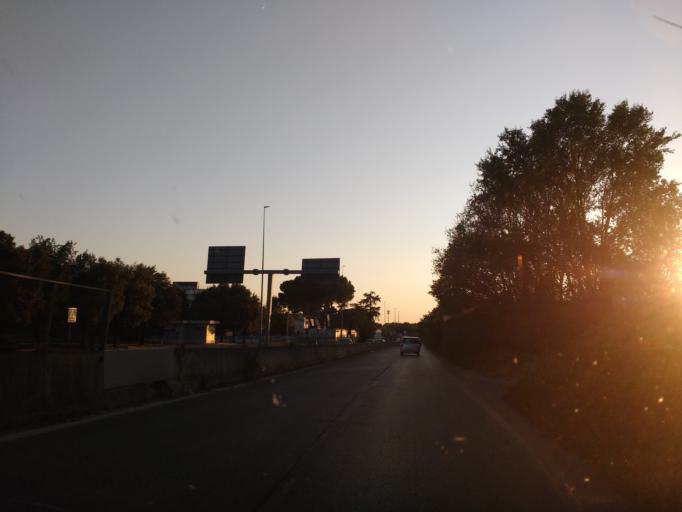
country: IT
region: Latium
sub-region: Citta metropolitana di Roma Capitale
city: Setteville
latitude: 41.9408
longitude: 12.6361
